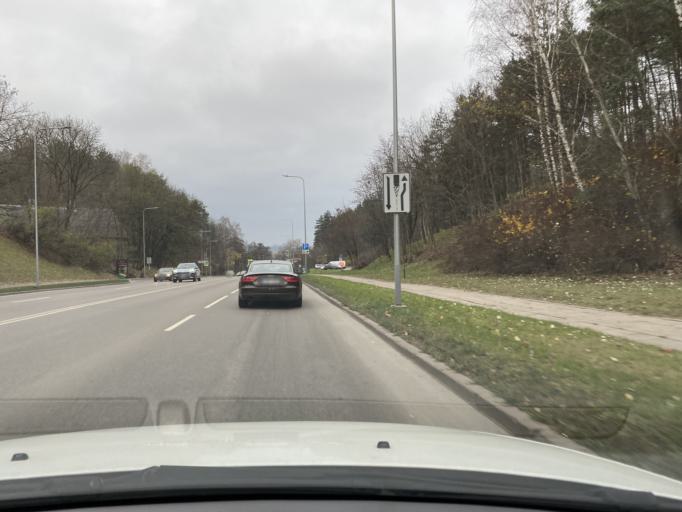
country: LT
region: Vilnius County
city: Rasos
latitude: 54.6867
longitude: 25.3065
